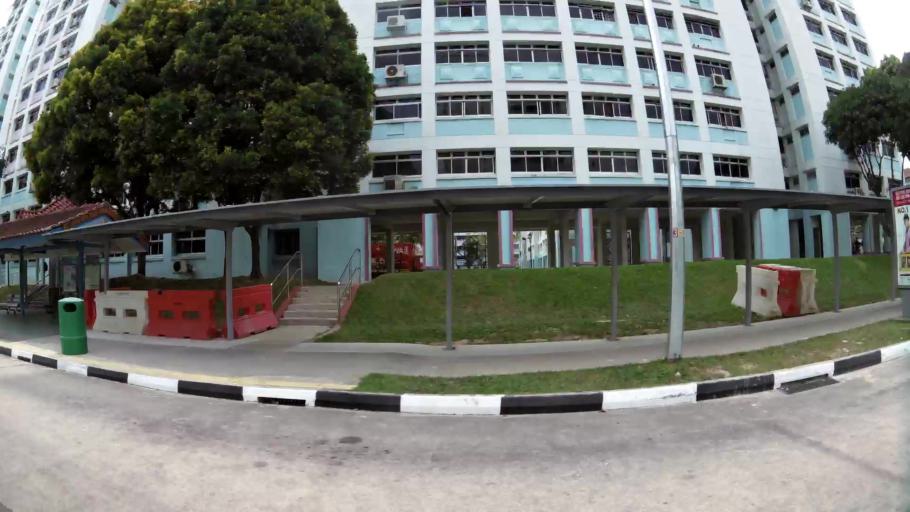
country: MY
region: Johor
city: Johor Bahru
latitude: 1.3485
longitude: 103.6961
